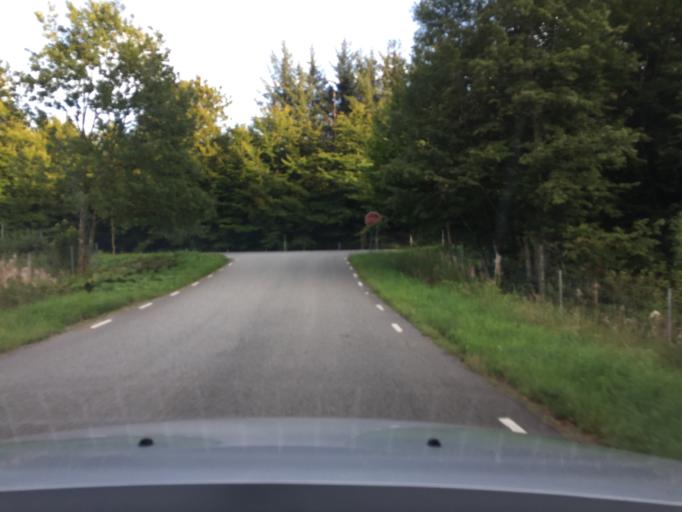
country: SE
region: Skane
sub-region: Hassleholms Kommun
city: Sosdala
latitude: 55.9844
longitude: 13.6044
